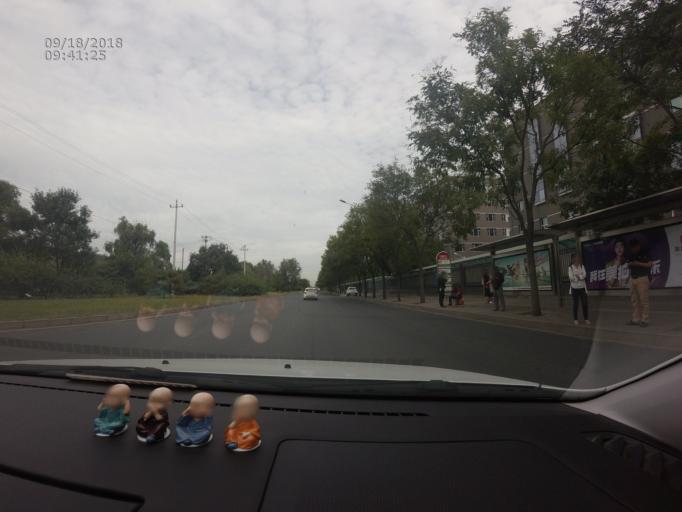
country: CN
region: Beijing
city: Xibeiwang
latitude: 40.0672
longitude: 116.2411
